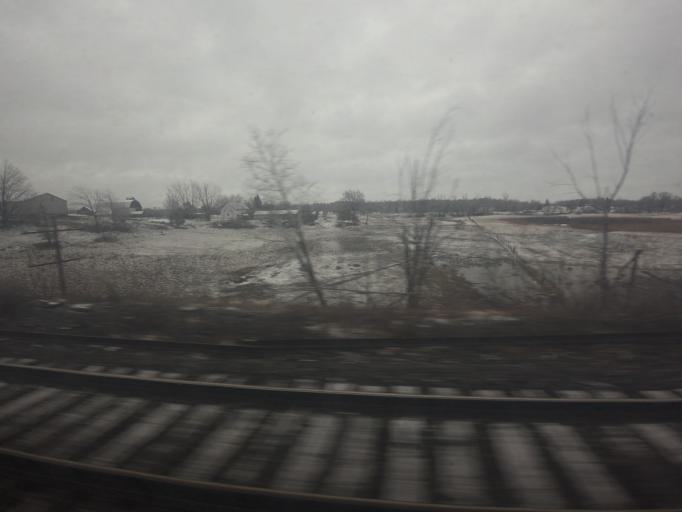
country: CA
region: Ontario
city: Gananoque
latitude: 44.3672
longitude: -76.1657
